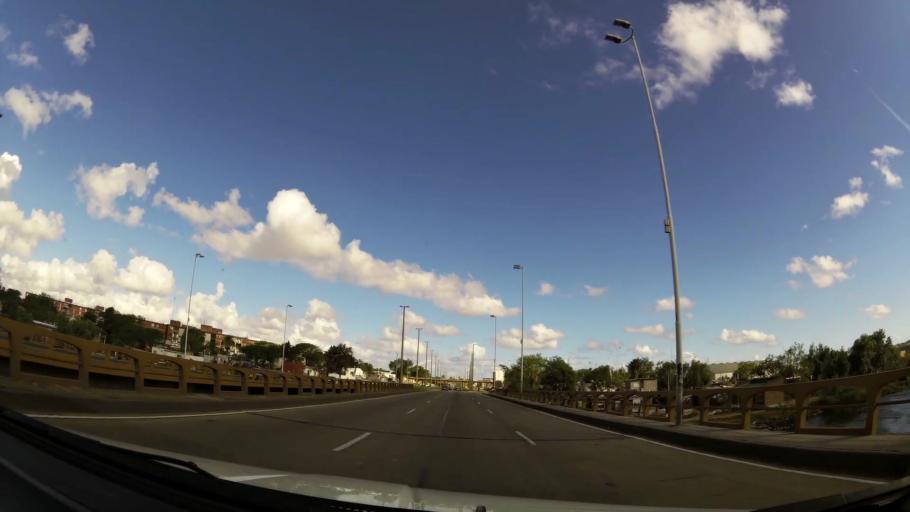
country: UY
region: Montevideo
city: Montevideo
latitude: -34.8685
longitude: -56.2446
